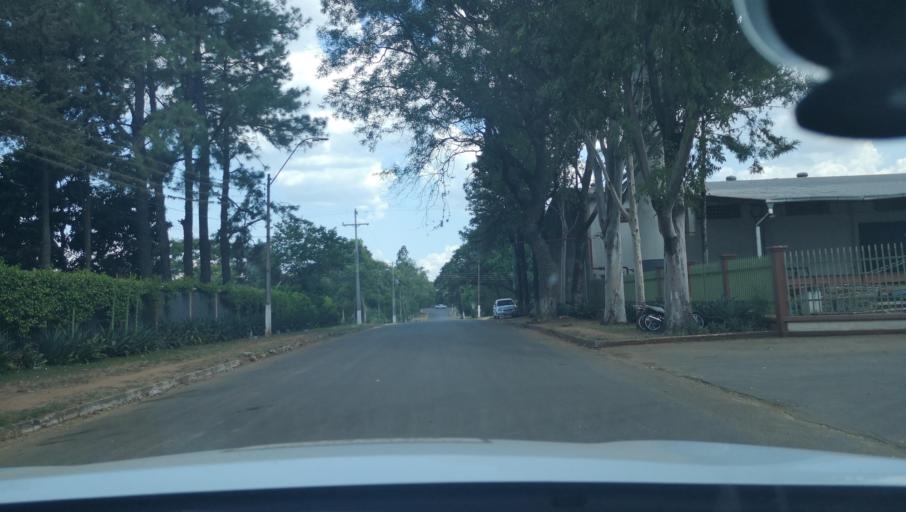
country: PY
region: Itapua
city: Carmen del Parana
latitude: -27.1536
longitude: -56.2477
